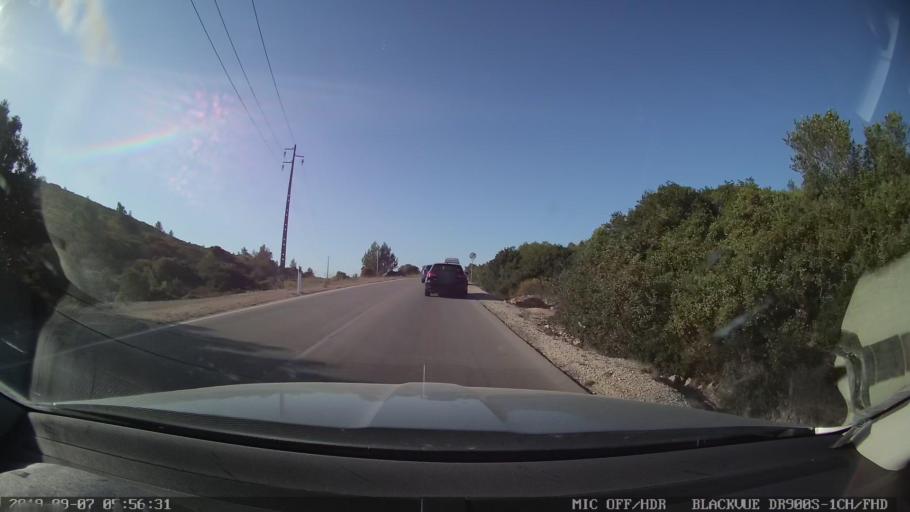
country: PT
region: Setubal
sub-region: Sesimbra
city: Sesimbra
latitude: 38.4453
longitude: -9.0869
